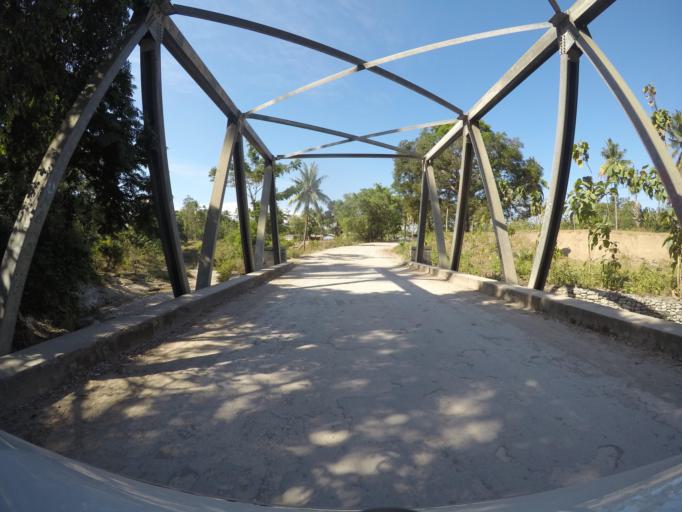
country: TL
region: Viqueque
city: Viqueque
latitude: -8.8604
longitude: 126.5083
